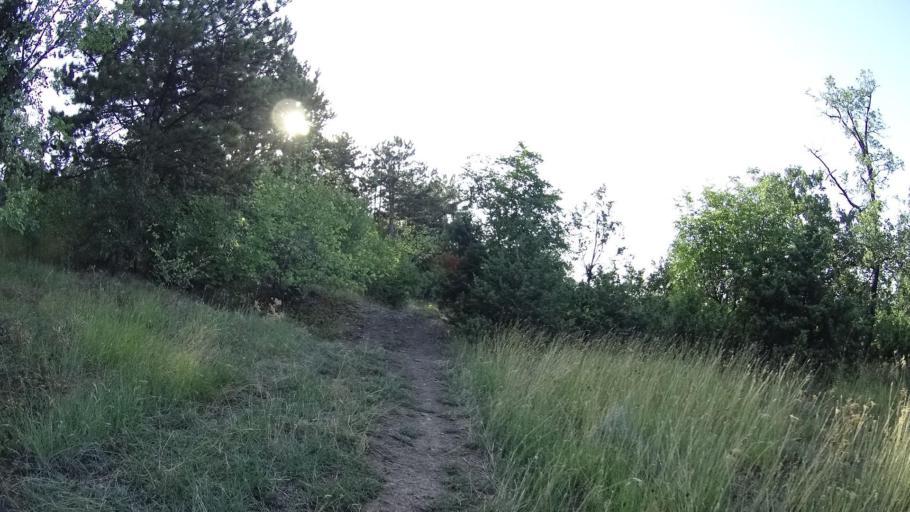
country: BG
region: Plovdiv
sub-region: Obshtina Plovdiv
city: Plovdiv
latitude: 42.0597
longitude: 24.6900
